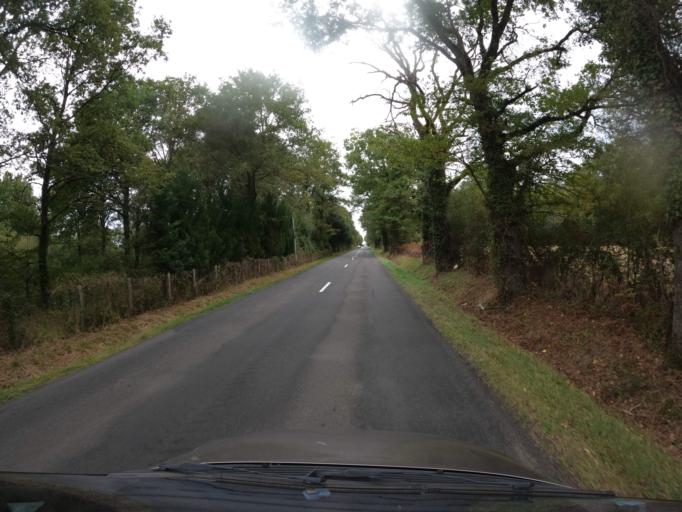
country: FR
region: Poitou-Charentes
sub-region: Departement de la Vienne
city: Saulge
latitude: 46.3465
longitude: 0.8295
